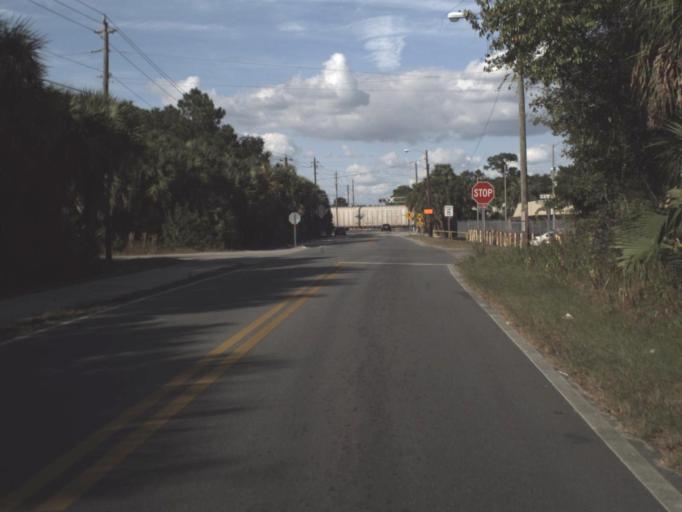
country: US
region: Florida
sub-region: Seminole County
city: Sanford
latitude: 28.8053
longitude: -81.2888
